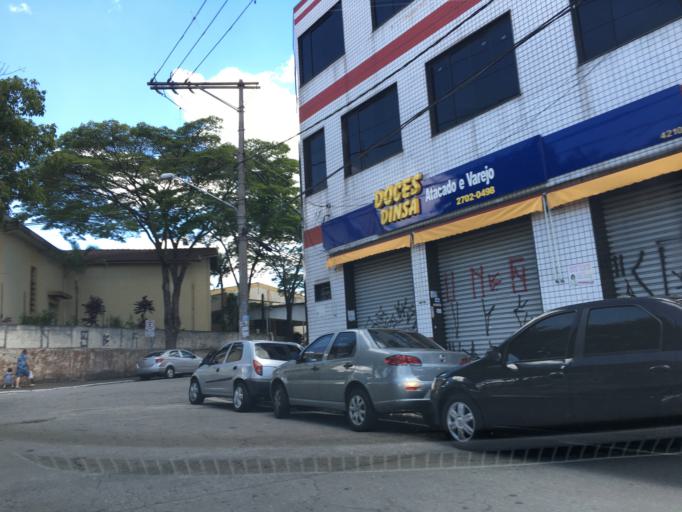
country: BR
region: Sao Paulo
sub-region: Sao Caetano Do Sul
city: Sao Caetano do Sul
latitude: -23.6017
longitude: -46.5339
